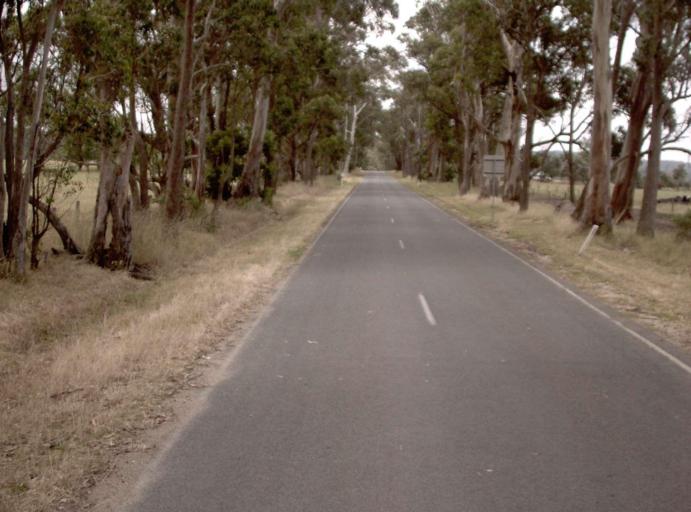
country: AU
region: Victoria
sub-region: Latrobe
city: Traralgon
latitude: -38.5139
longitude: 146.6487
